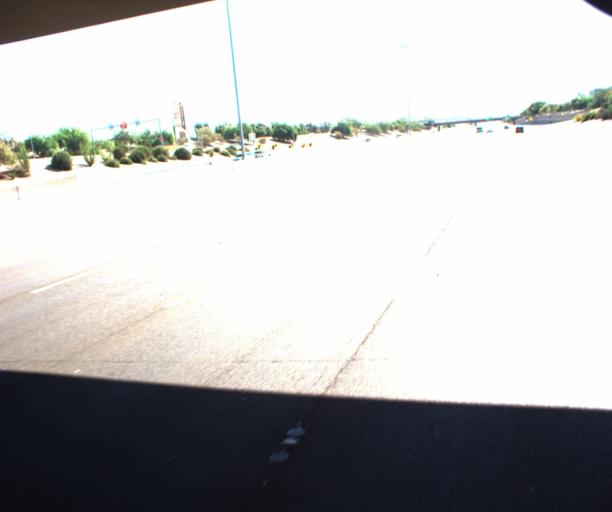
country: US
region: Arizona
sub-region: Maricopa County
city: Gilbert
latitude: 33.3864
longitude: -111.6847
